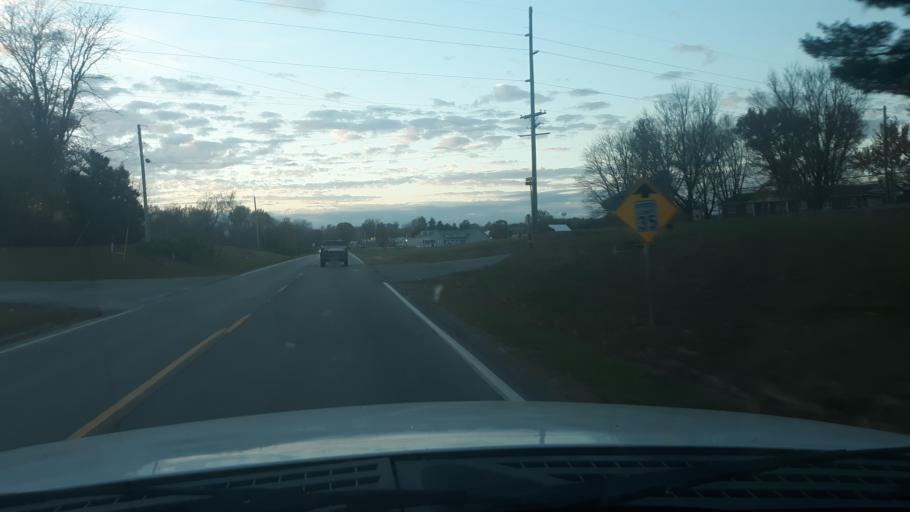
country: US
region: Illinois
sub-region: Saline County
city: Harrisburg
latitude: 37.8377
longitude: -88.5958
